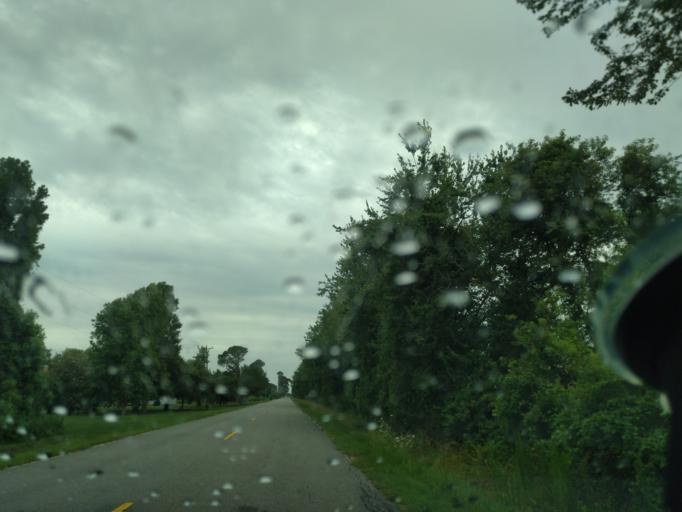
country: US
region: North Carolina
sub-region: Beaufort County
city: Belhaven
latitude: 35.7640
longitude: -76.5232
